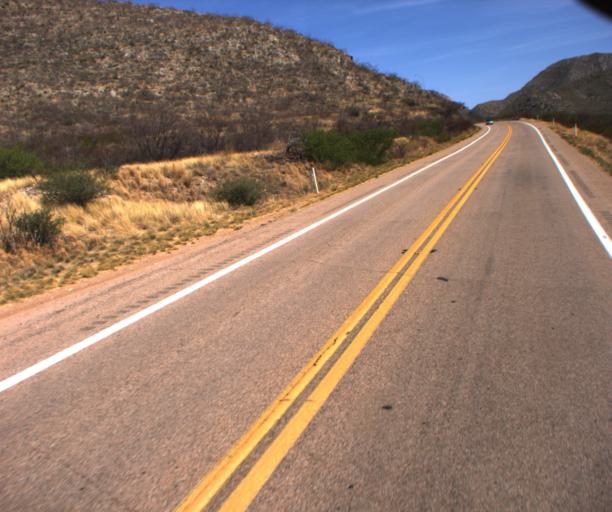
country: US
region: Arizona
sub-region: Cochise County
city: Bisbee
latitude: 31.5194
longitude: -110.0302
